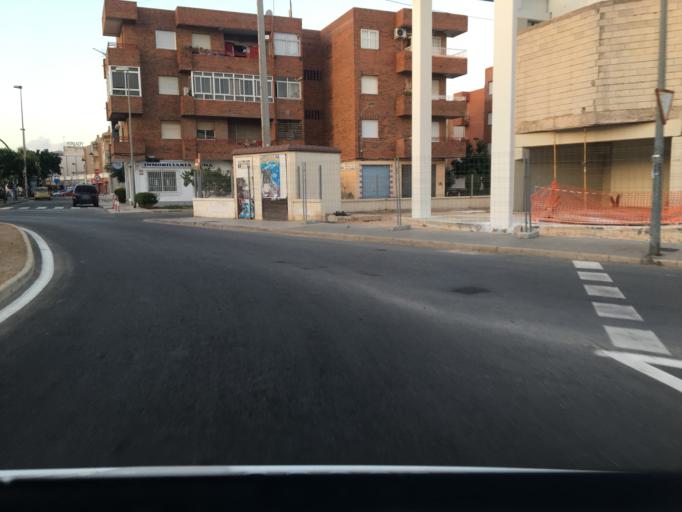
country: ES
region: Murcia
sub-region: Murcia
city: Cartagena
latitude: 37.6272
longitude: -1.0020
